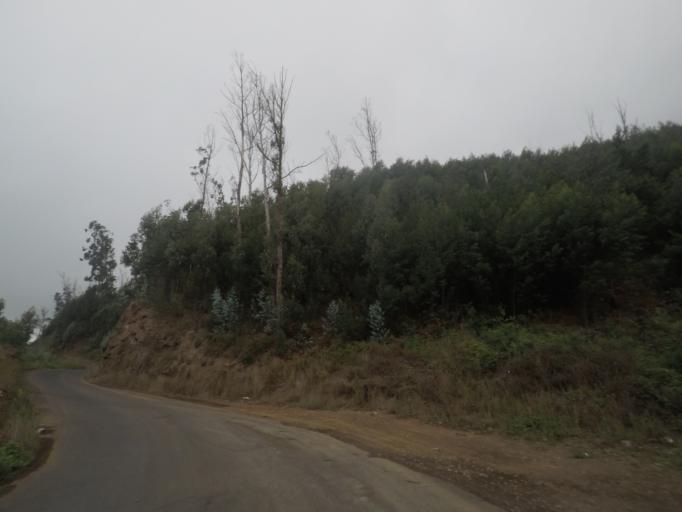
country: PT
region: Madeira
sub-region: Funchal
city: Nossa Senhora do Monte
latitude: 32.6902
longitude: -16.9037
